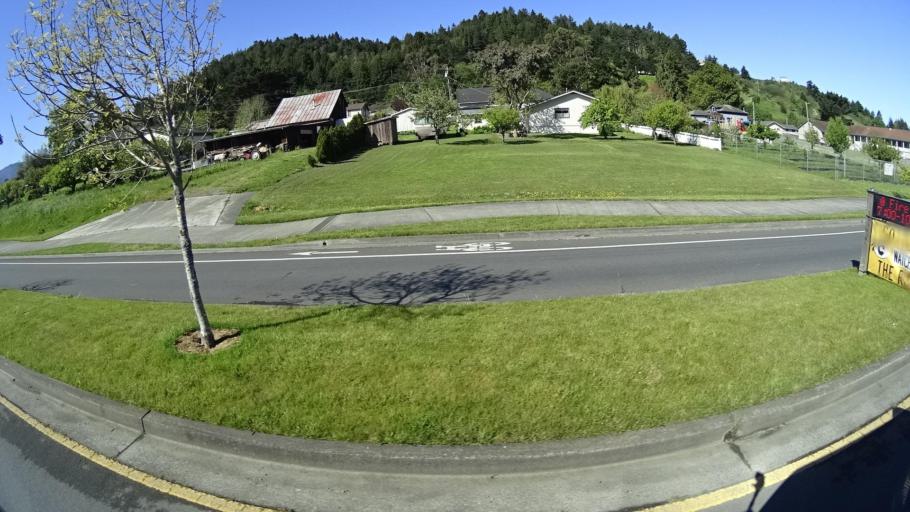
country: US
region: California
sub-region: Humboldt County
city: Rio Dell
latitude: 40.5035
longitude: -124.1075
